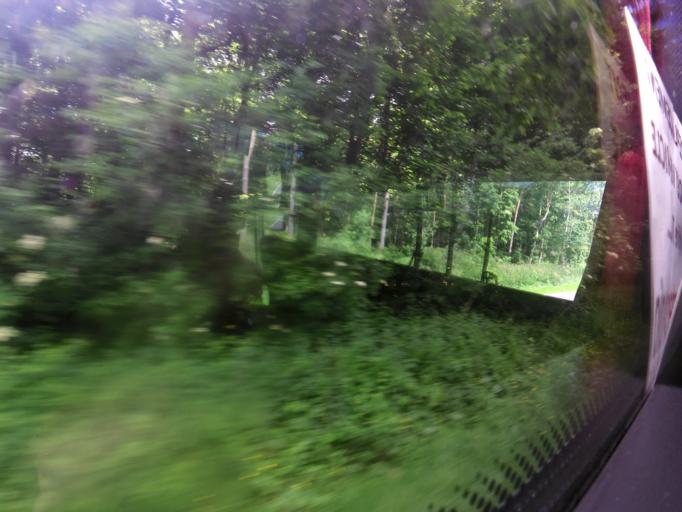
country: GB
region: England
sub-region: Norfolk
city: Cromer
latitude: 52.9181
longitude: 1.2623
